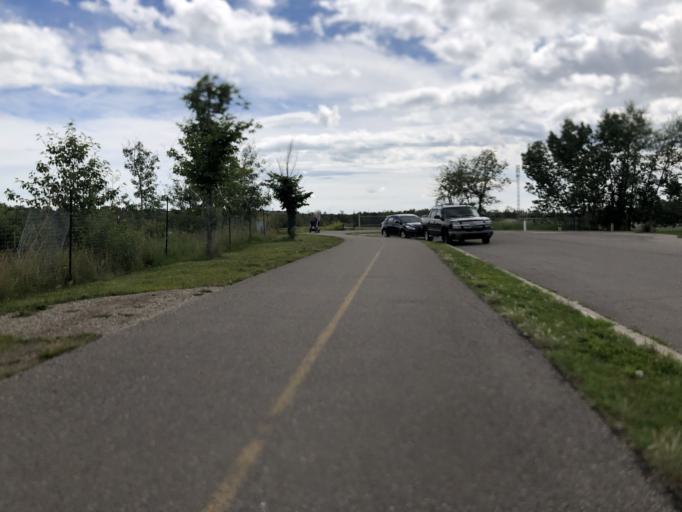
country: CA
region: Alberta
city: Calgary
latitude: 51.0328
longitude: -114.0117
